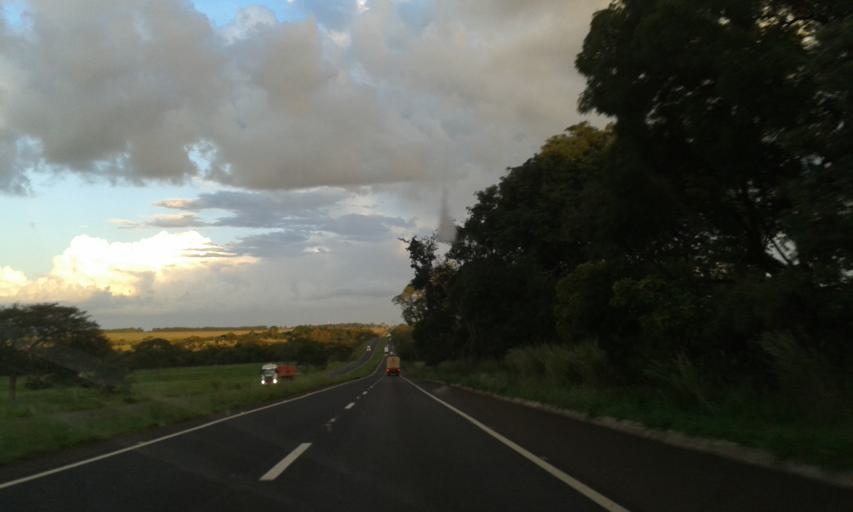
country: BR
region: Minas Gerais
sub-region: Monte Alegre De Minas
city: Monte Alegre de Minas
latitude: -18.8563
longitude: -48.7757
